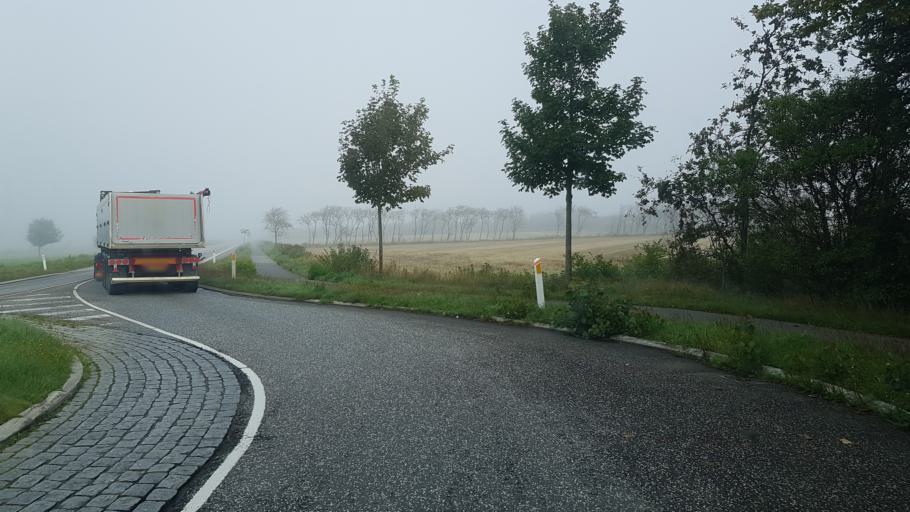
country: DK
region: Central Jutland
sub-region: Viborg Kommune
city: Karup
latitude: 56.3249
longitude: 9.2648
